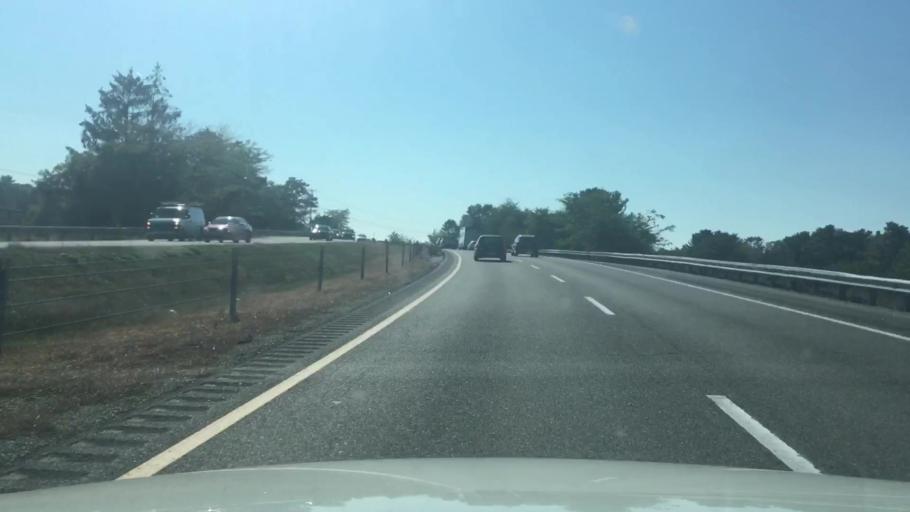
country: US
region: Maine
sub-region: Cumberland County
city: Yarmouth
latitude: 43.8095
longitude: -70.1649
